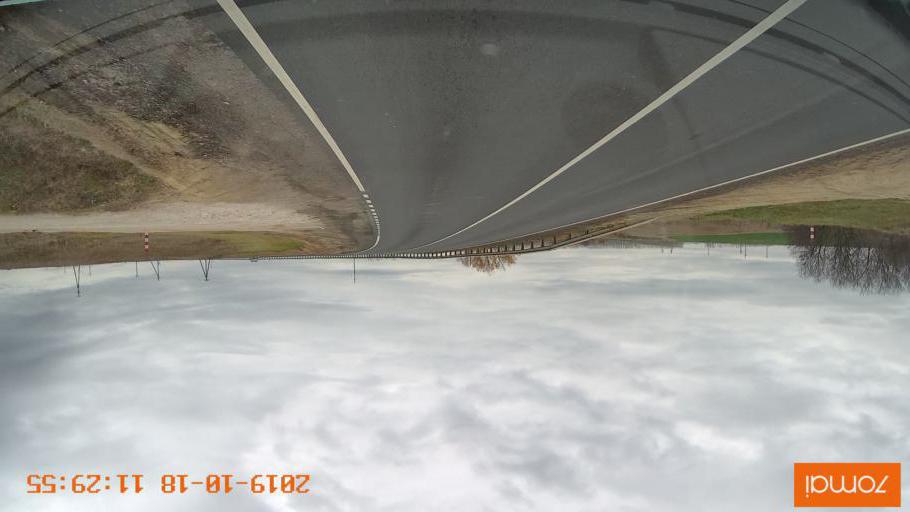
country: RU
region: Rjazan
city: Oktyabr'skiy
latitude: 54.1567
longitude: 38.6837
